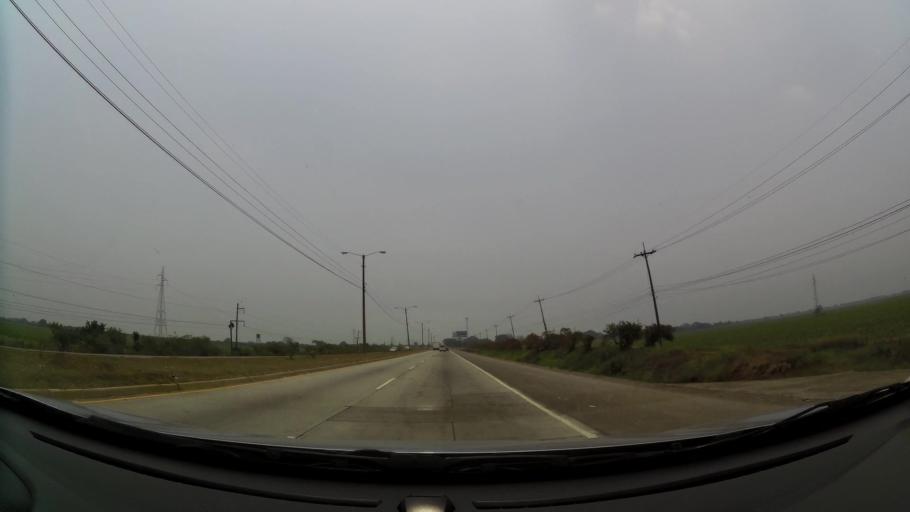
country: HN
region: Yoro
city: El Progreso
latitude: 15.4118
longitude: -87.8589
